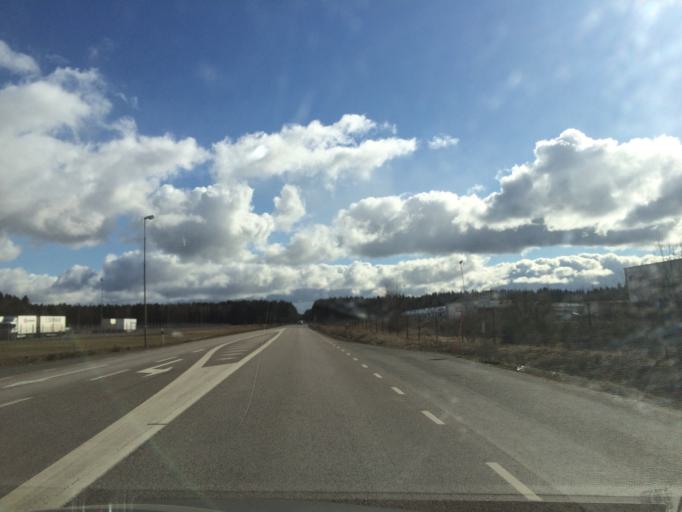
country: SE
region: Vaestra Goetaland
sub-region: Skara Kommun
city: Skara
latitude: 58.3728
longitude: 13.4150
